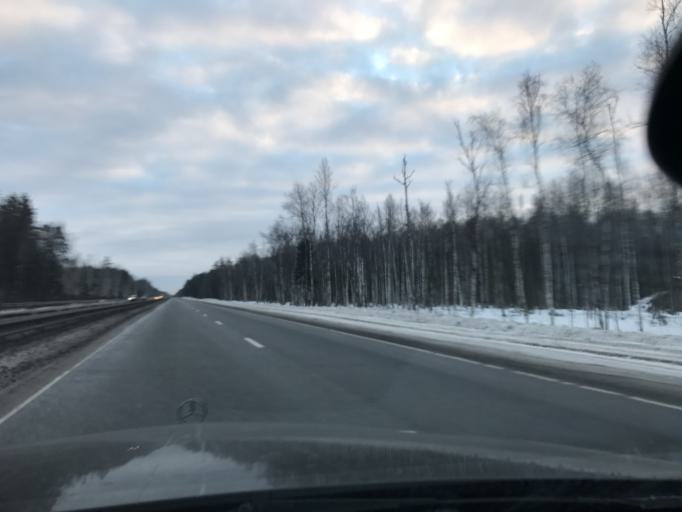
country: RU
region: Vladimir
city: Stepantsevo
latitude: 56.2339
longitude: 41.8258
